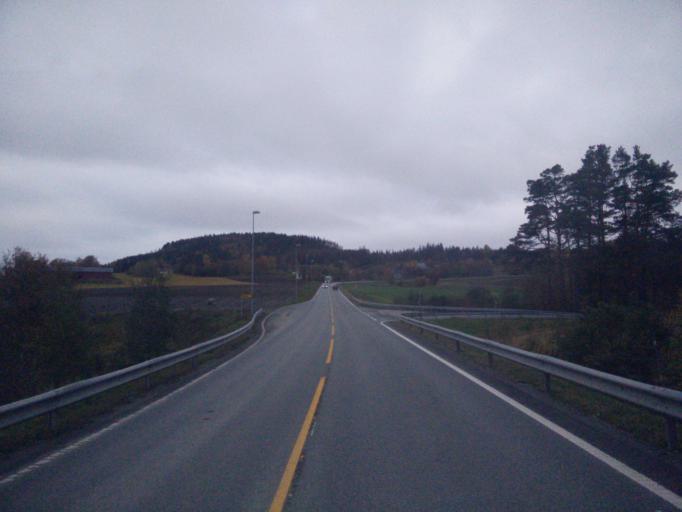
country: NO
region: Nord-Trondelag
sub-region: Stjordal
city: Stjordal
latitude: 63.5057
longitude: 10.8571
